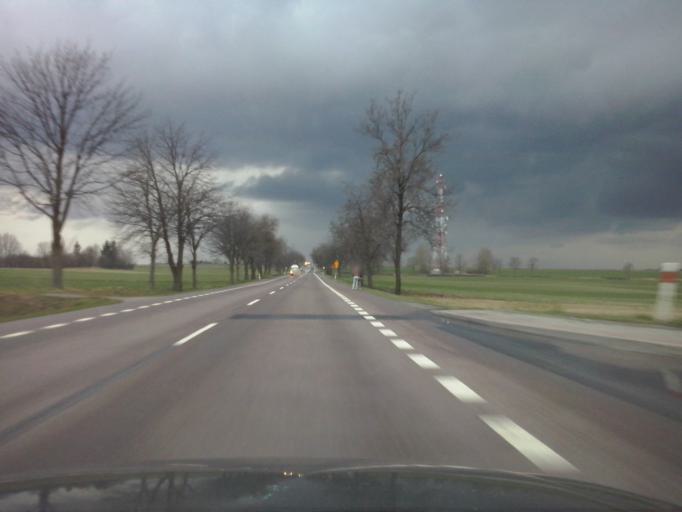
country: PL
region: Lublin Voivodeship
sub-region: Powiat chelmski
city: Rejowiec Fabryczny
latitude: 51.1771
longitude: 23.2279
